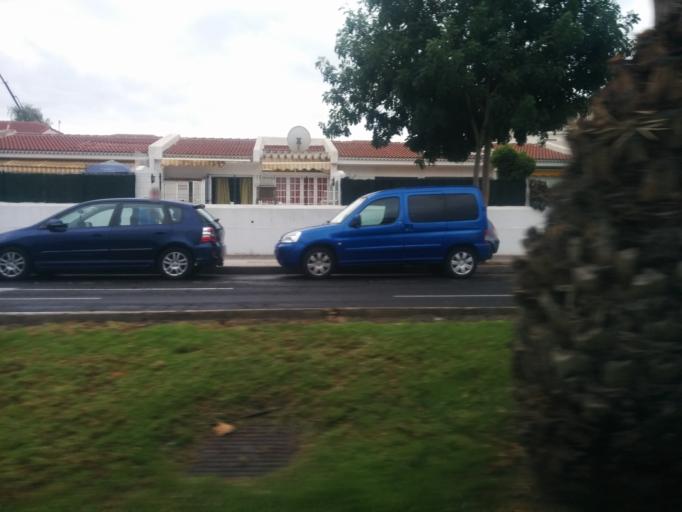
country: ES
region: Canary Islands
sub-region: Provincia de Santa Cruz de Tenerife
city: Playa de las Americas
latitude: 28.0793
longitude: -16.7314
